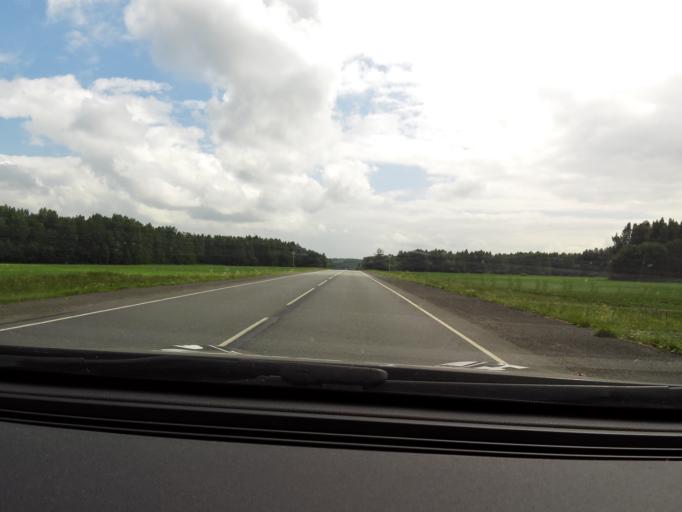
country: RU
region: Perm
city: Orda
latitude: 57.1887
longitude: 57.1211
